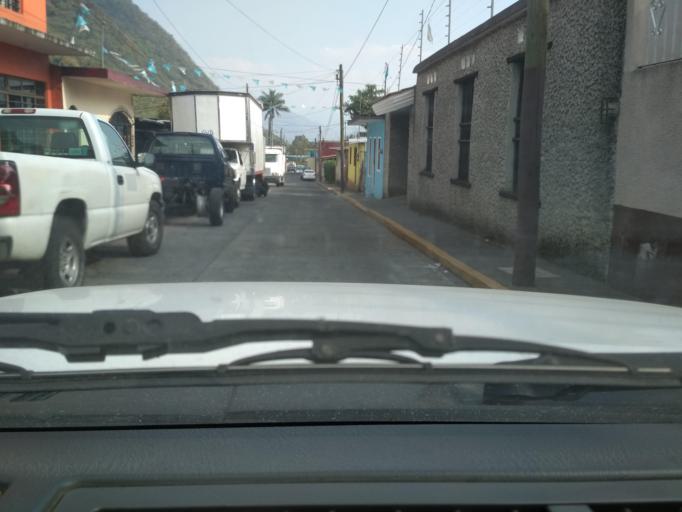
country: MX
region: Veracruz
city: Orizaba
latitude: 18.8681
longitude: -97.0956
